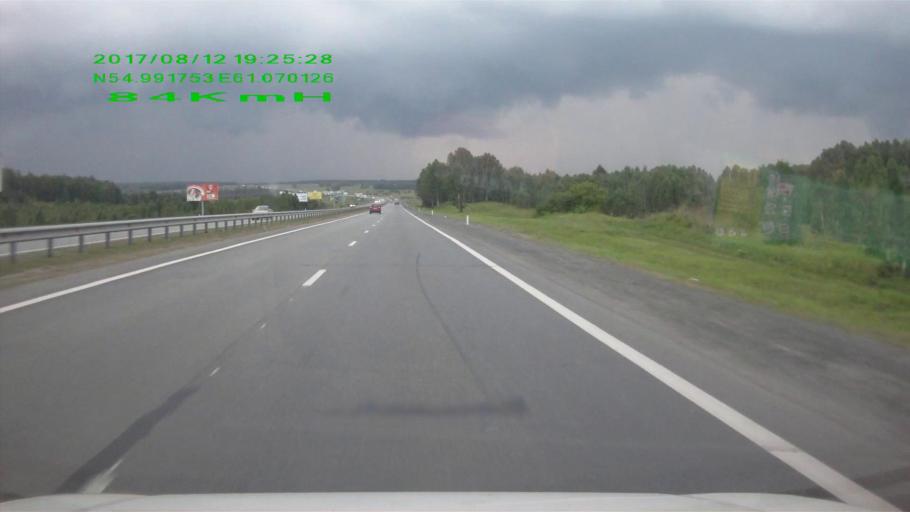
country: RU
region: Chelyabinsk
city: Poletayevo
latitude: 54.9916
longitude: 61.0666
